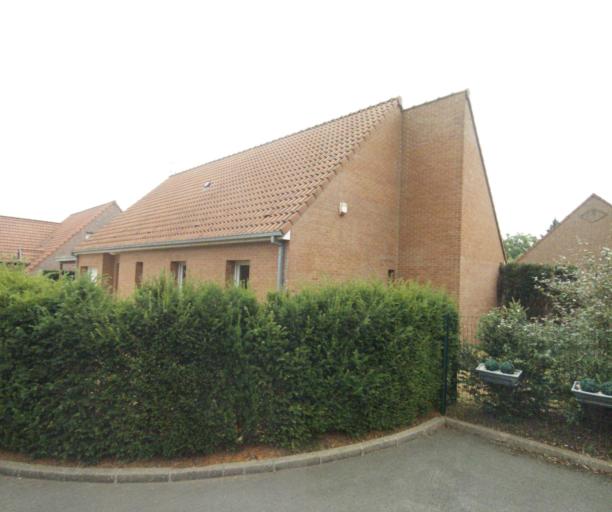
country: FR
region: Nord-Pas-de-Calais
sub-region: Departement du Nord
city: Leers
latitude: 50.6872
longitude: 3.2413
